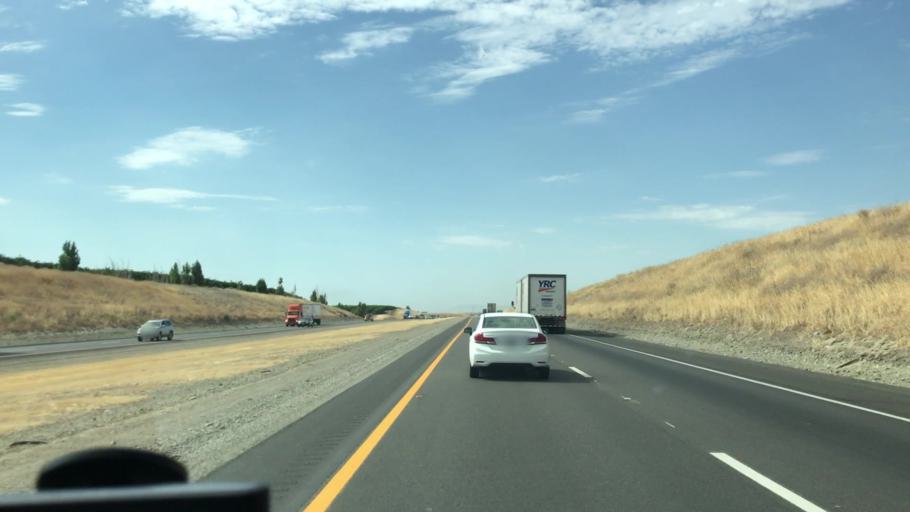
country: US
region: California
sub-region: Stanislaus County
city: Newman
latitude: 37.3475
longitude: -121.1173
